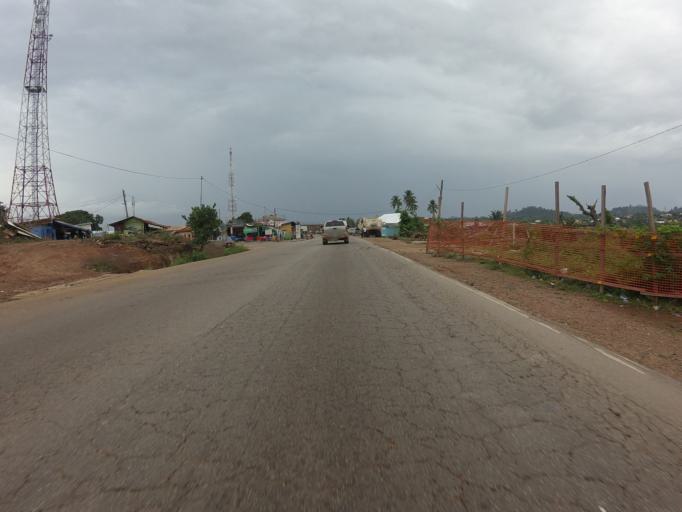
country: GH
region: Ashanti
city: Konongo
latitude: 6.6249
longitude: -1.2055
